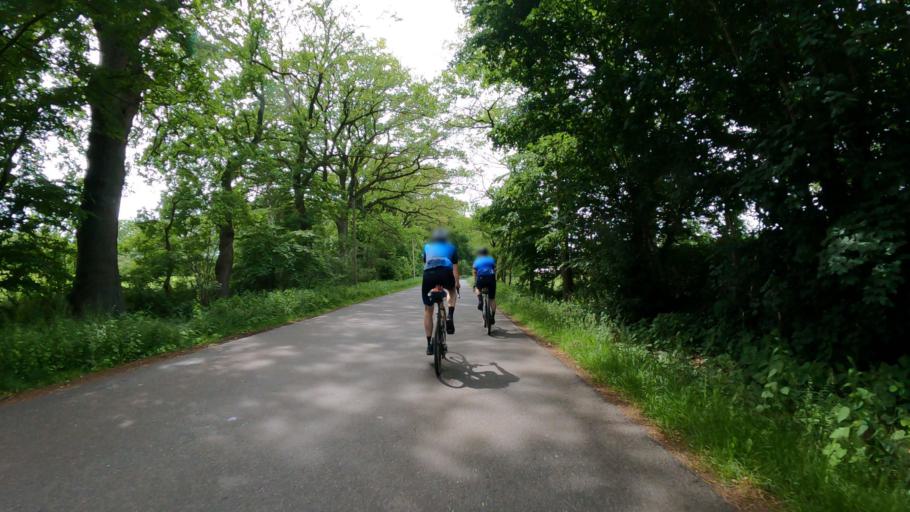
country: DE
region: Schleswig-Holstein
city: Tangstedt
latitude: 53.7436
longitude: 10.0328
